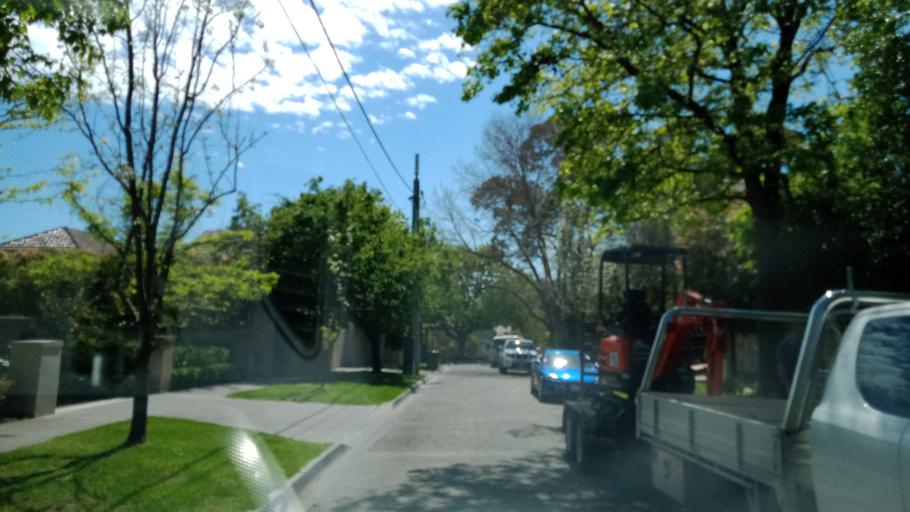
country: AU
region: Victoria
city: Toorak
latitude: -37.8412
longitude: 145.0286
